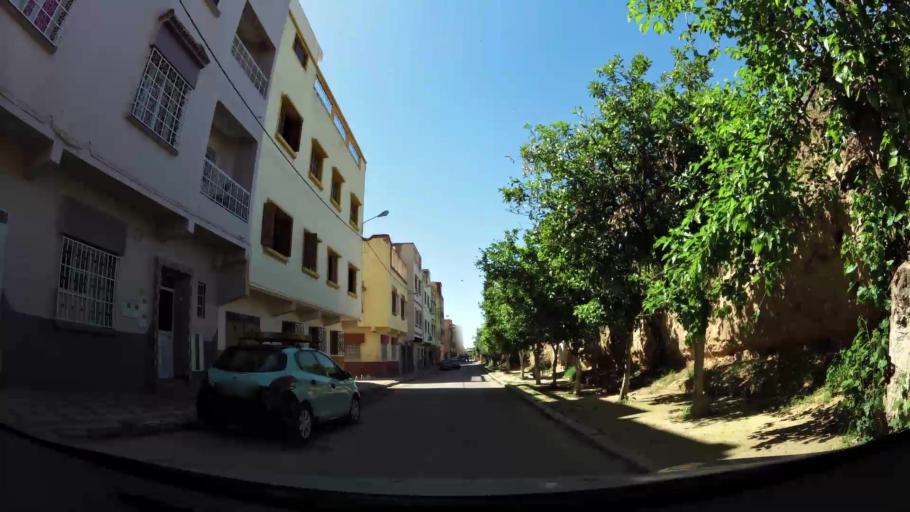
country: MA
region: Meknes-Tafilalet
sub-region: Meknes
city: Meknes
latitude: 33.8806
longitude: -5.5606
